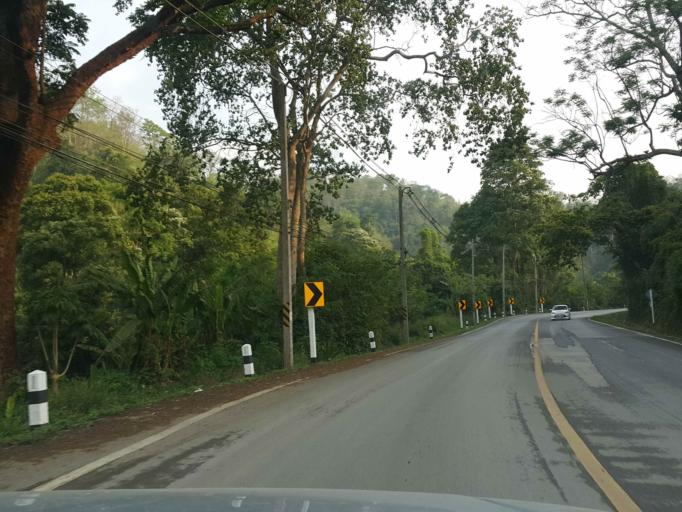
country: TH
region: Chiang Mai
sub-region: Amphoe Chiang Dao
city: Chiang Dao
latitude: 19.2827
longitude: 98.9685
